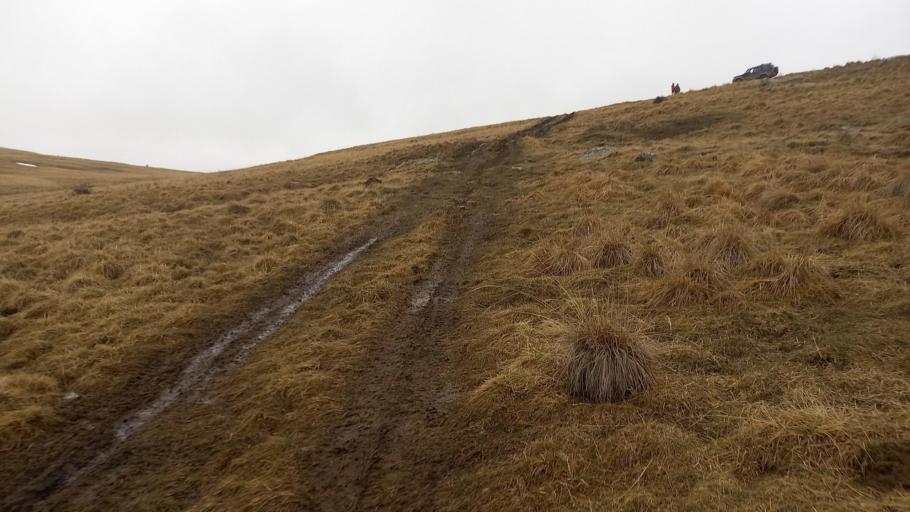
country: RU
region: Kabardino-Balkariya
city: Terskol
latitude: 43.5214
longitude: 42.4258
